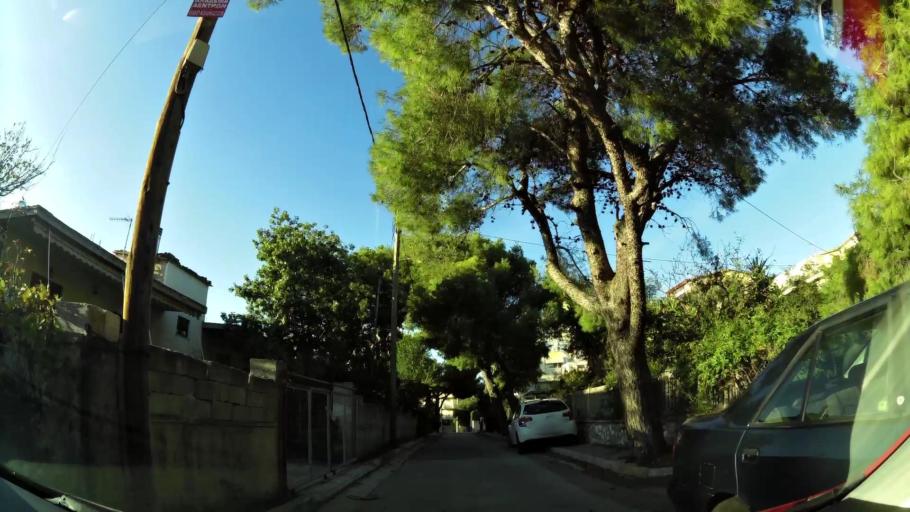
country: GR
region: Attica
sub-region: Nomarchia Anatolikis Attikis
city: Rafina
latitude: 38.0119
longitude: 24.0136
